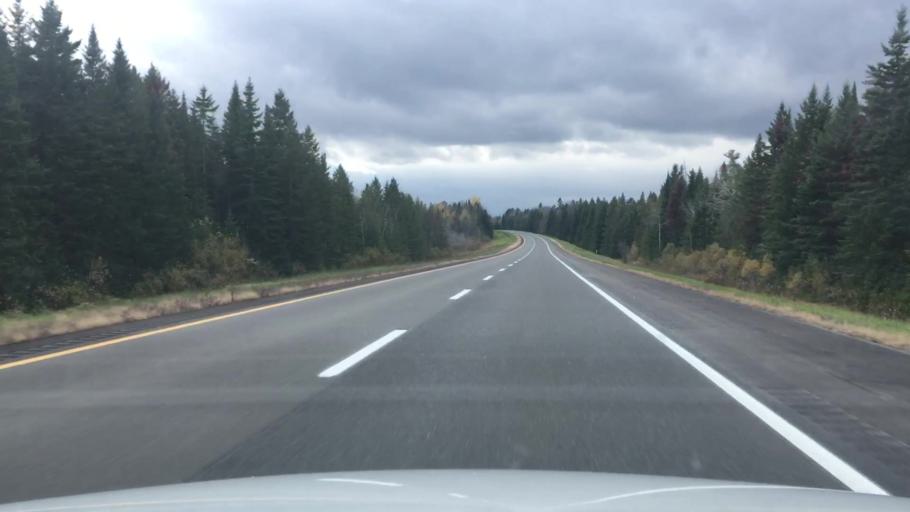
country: US
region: Maine
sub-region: Penobscot County
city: Patten
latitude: 46.0937
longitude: -68.1964
